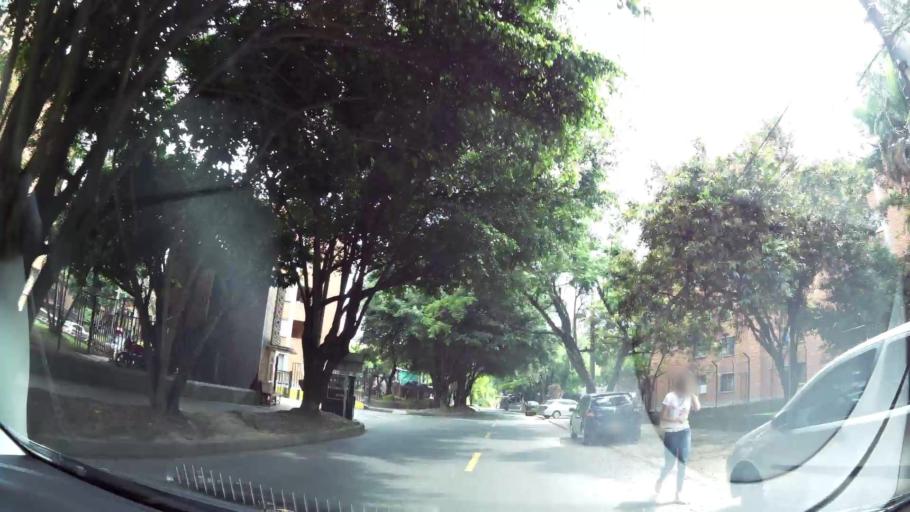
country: CO
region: Antioquia
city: Itagui
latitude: 6.1954
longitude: -75.5942
